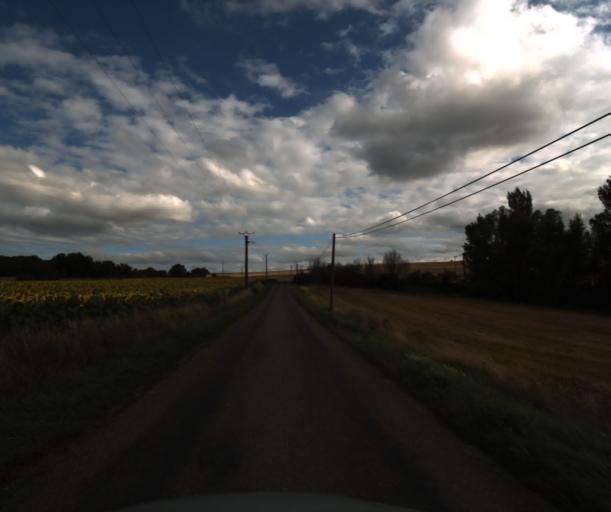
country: FR
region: Midi-Pyrenees
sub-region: Departement de la Haute-Garonne
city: Le Fauga
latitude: 43.4070
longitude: 1.3209
